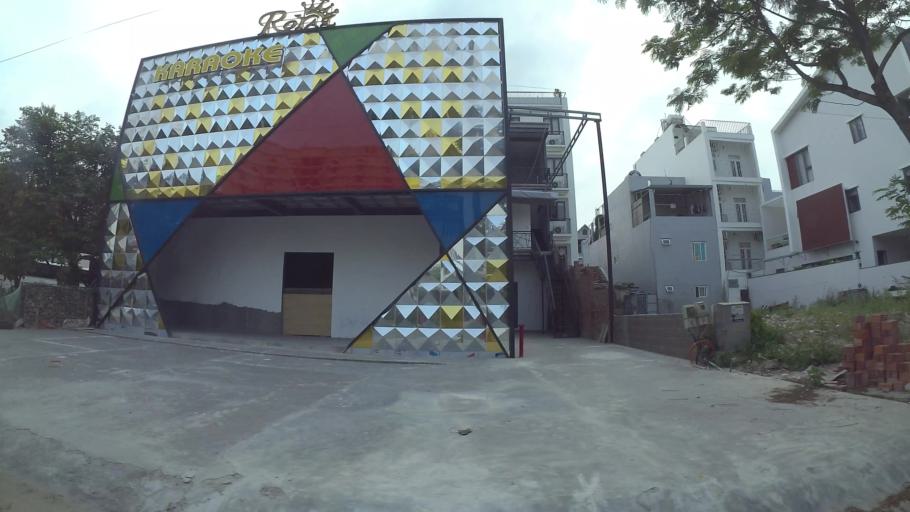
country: VN
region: Da Nang
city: Son Tra
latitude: 16.0581
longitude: 108.2449
